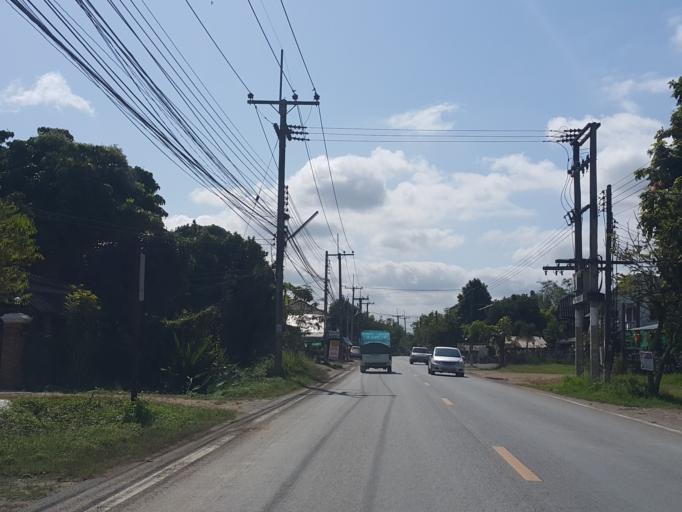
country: TH
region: Chiang Mai
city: San Kamphaeng
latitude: 18.6966
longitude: 99.1602
